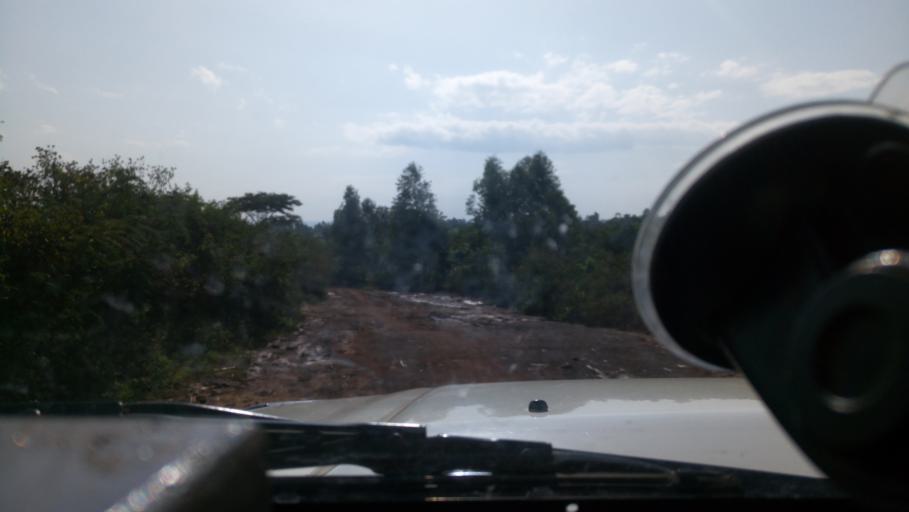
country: KE
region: Migori
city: Migori
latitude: -1.0466
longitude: 34.5448
